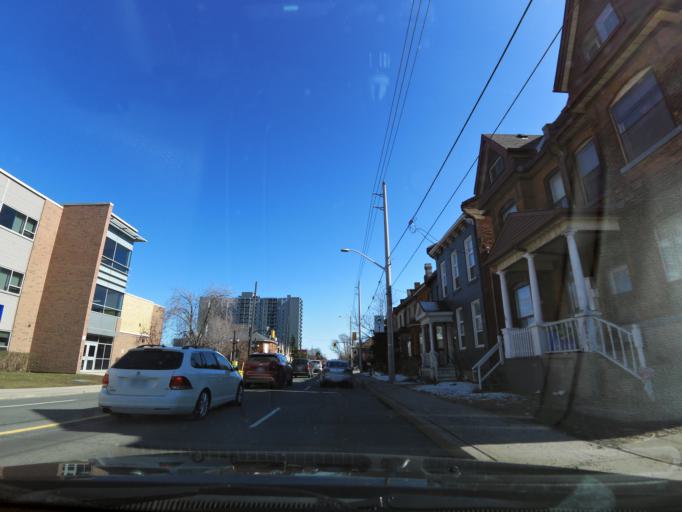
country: CA
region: Ontario
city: Hamilton
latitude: 43.2574
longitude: -79.8619
